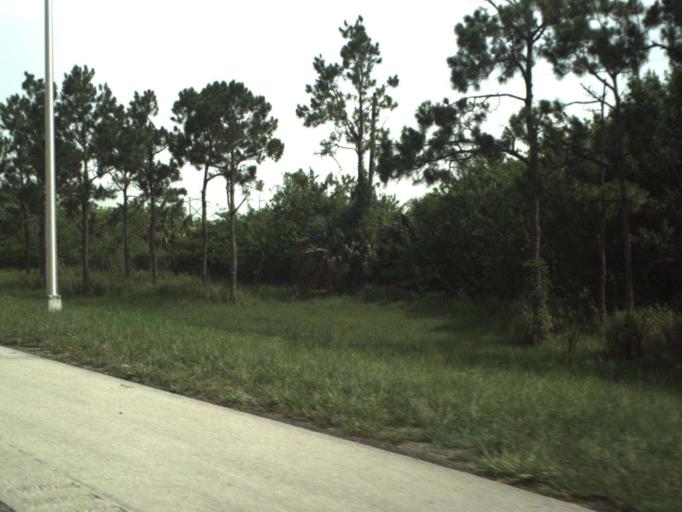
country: US
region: Florida
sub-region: Saint Lucie County
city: Lakewood Park
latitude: 27.5300
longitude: -80.4577
